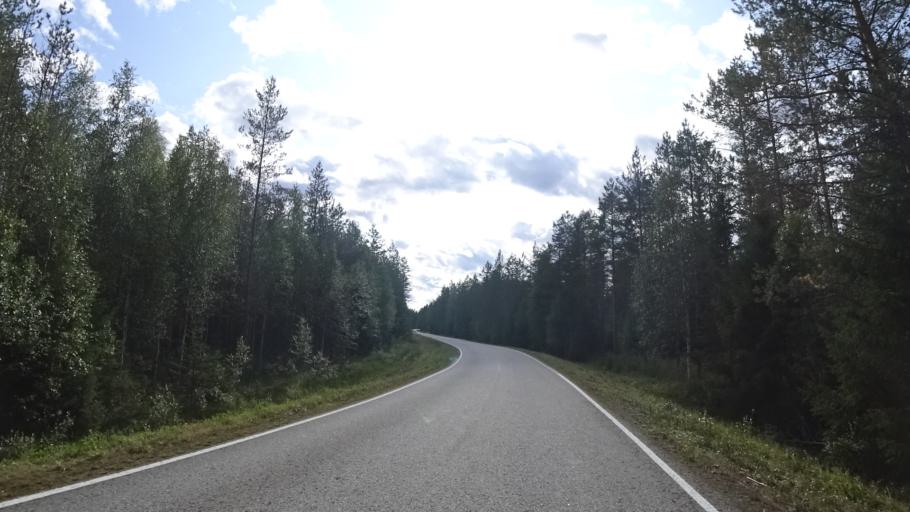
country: RU
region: Republic of Karelia
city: Vyartsilya
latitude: 62.2365
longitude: 30.6915
